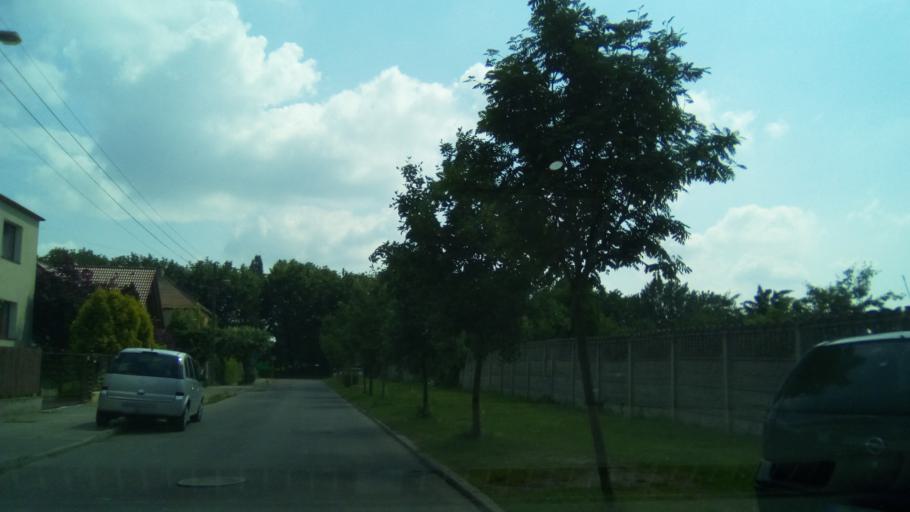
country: PL
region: Greater Poland Voivodeship
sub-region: Powiat gnieznienski
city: Gniezno
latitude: 52.5332
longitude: 17.6141
